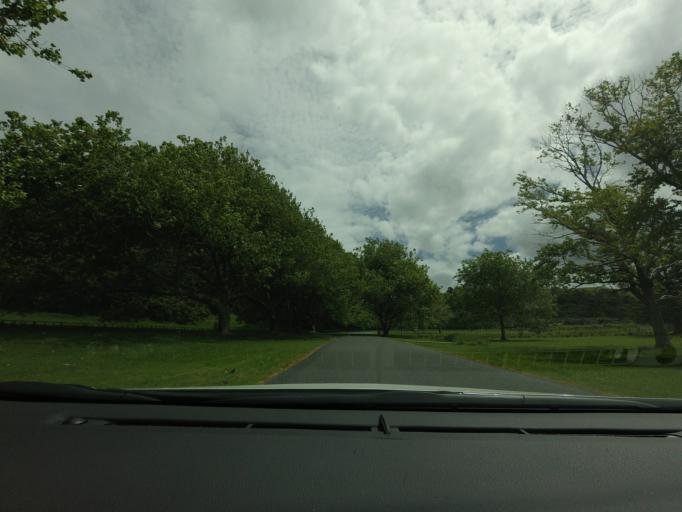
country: NZ
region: Auckland
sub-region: Auckland
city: Warkworth
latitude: -36.5349
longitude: 174.7075
